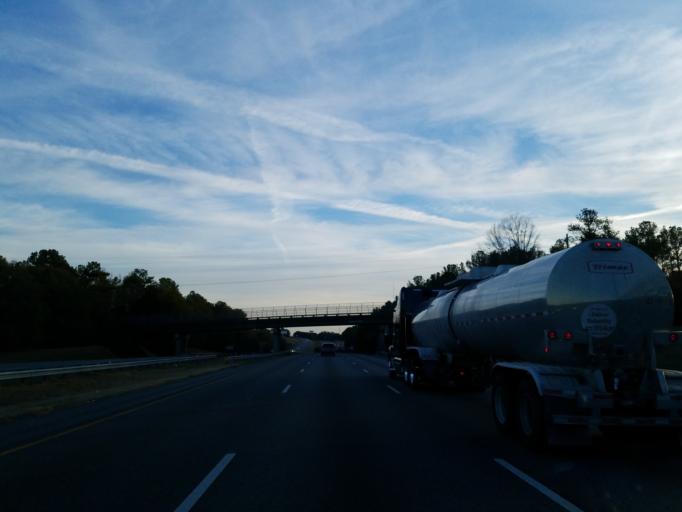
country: US
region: Georgia
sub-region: Bartow County
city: Adairsville
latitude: 34.4034
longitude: -84.9193
